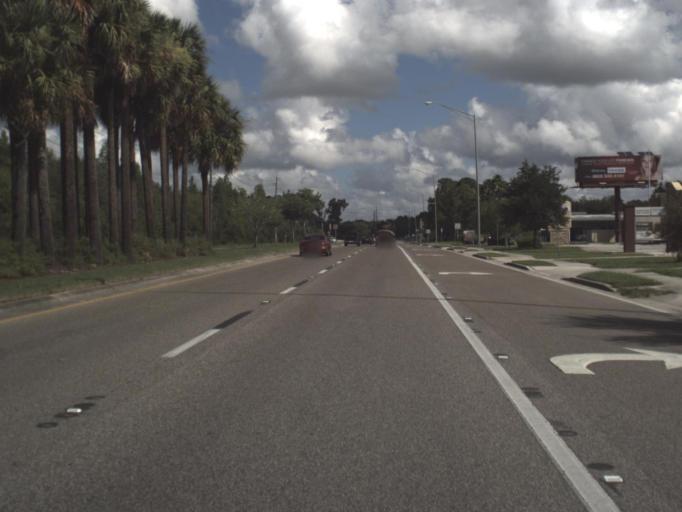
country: US
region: Florida
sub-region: Polk County
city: Lakeland
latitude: 28.0203
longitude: -81.9735
